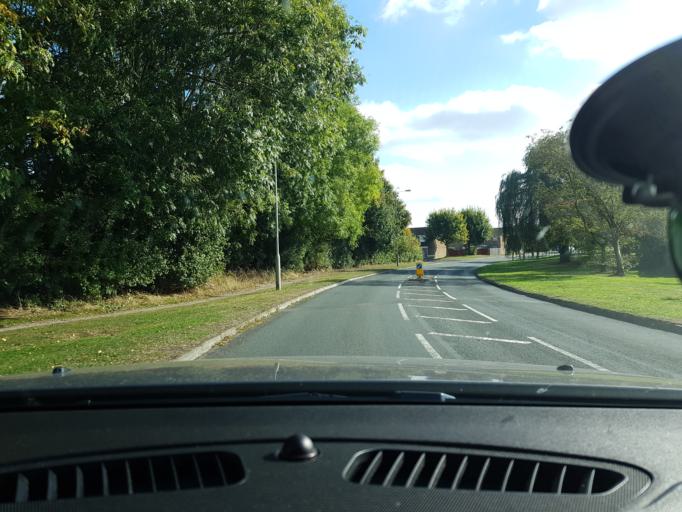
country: GB
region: England
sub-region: Borough of Swindon
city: Wanborough
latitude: 51.5470
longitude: -1.7273
